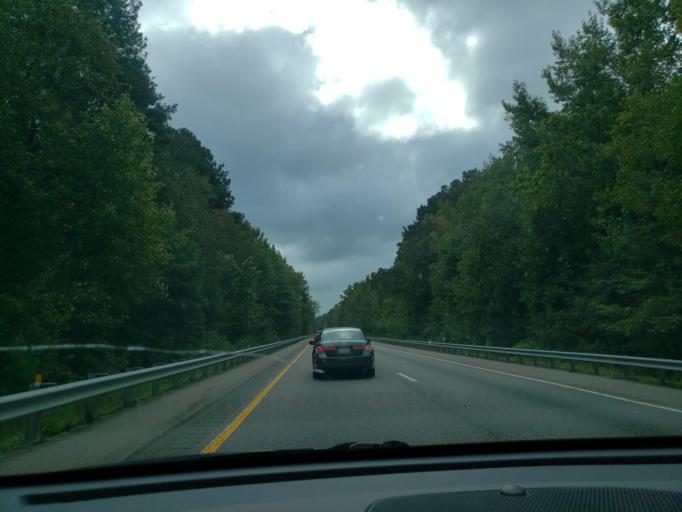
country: US
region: Virginia
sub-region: Mecklenburg County
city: South Hill
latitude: 36.6757
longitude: -78.1295
